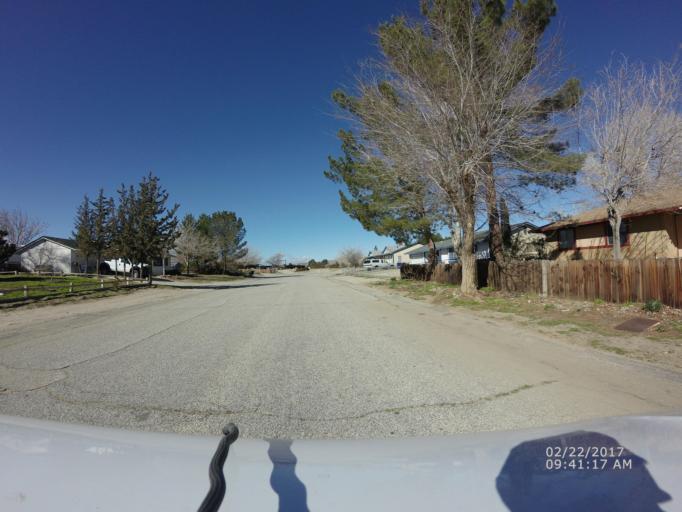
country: US
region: California
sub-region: Los Angeles County
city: Lake Los Angeles
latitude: 34.6252
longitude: -117.8422
